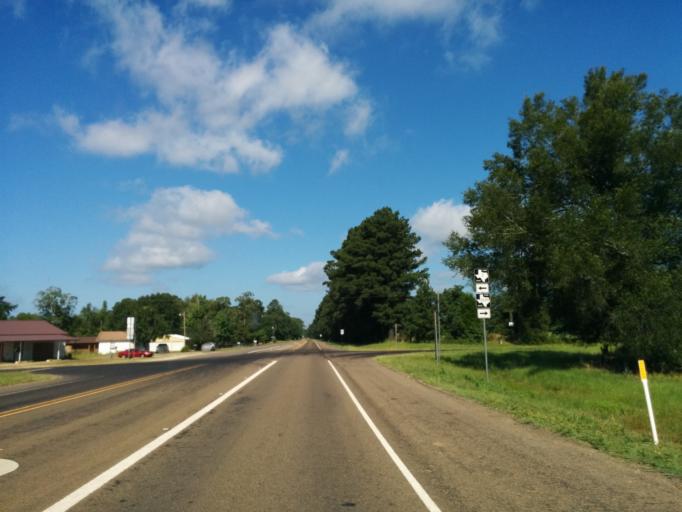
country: US
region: Texas
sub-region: Sabine County
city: Milam
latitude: 31.4126
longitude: -93.9975
